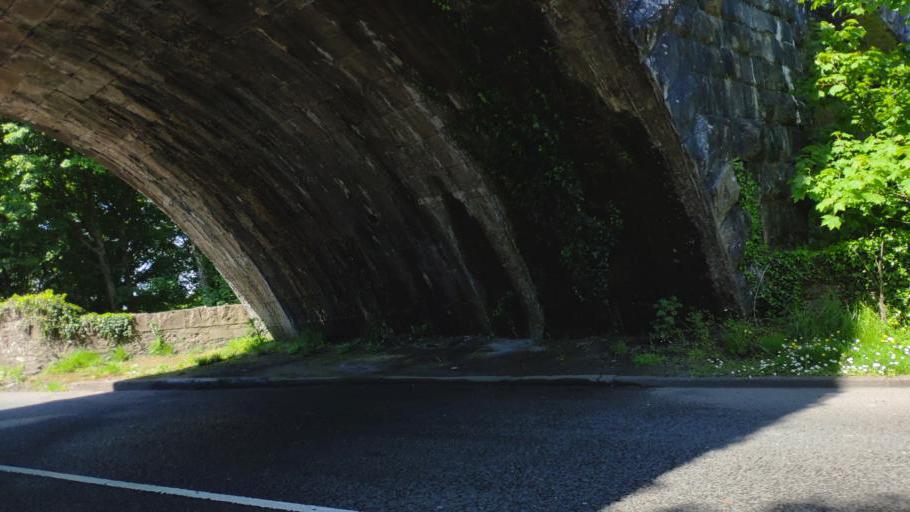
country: IE
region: Munster
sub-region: County Cork
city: Cork
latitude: 51.9264
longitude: -8.4870
